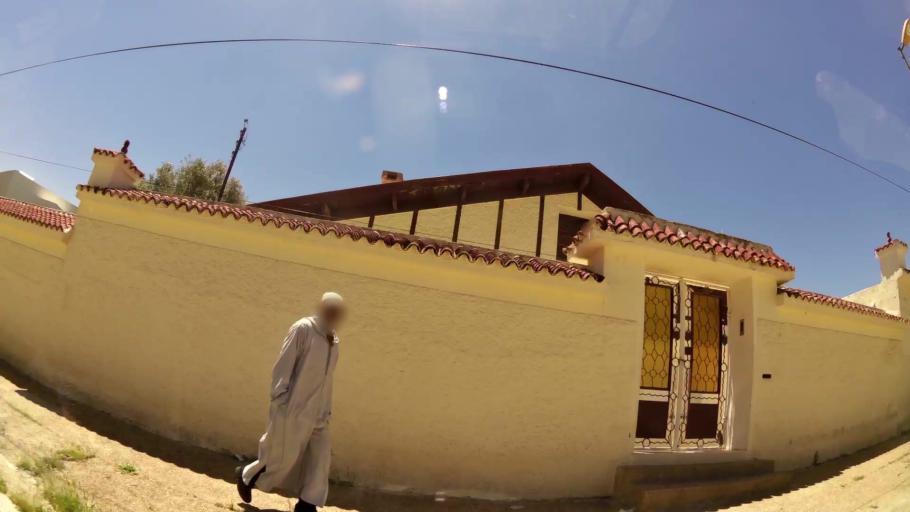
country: MA
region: Meknes-Tafilalet
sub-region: Meknes
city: Meknes
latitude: 33.9099
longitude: -5.5634
